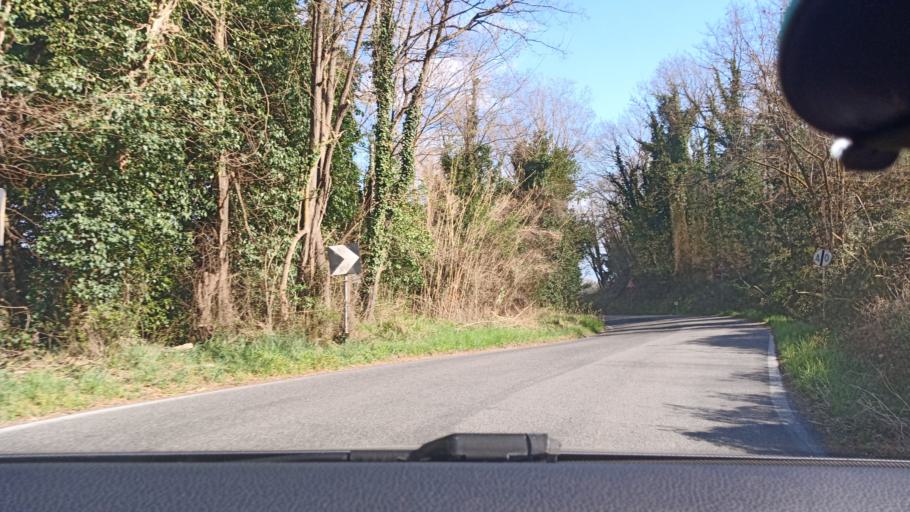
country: IT
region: Latium
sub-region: Citta metropolitana di Roma Capitale
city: Torrita Tiberina
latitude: 42.2484
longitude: 12.6174
